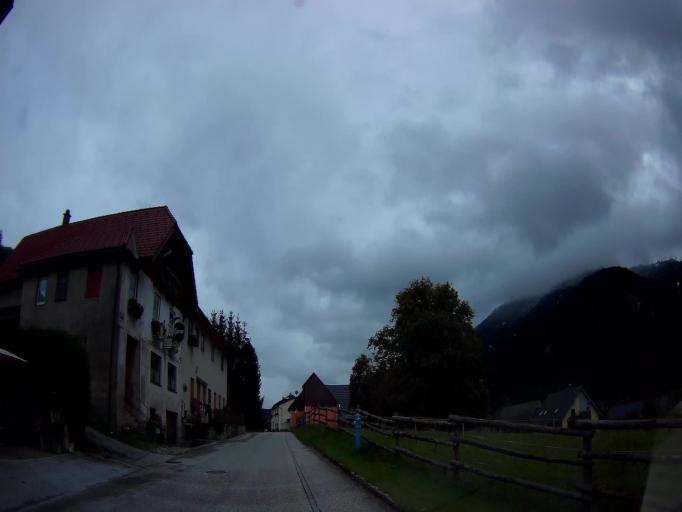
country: AT
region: Styria
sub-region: Politischer Bezirk Liezen
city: Treglwang
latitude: 47.4759
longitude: 14.5893
